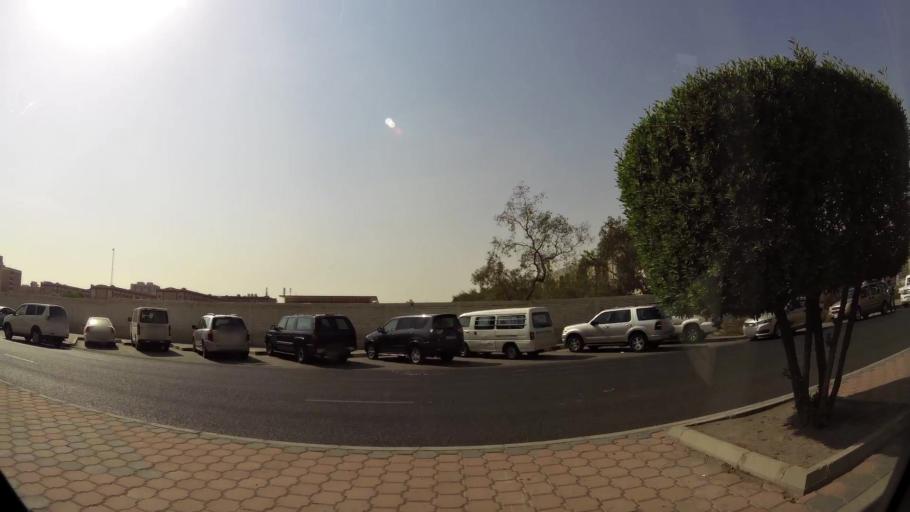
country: KW
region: Al Ahmadi
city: Al Manqaf
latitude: 29.0902
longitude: 48.1302
